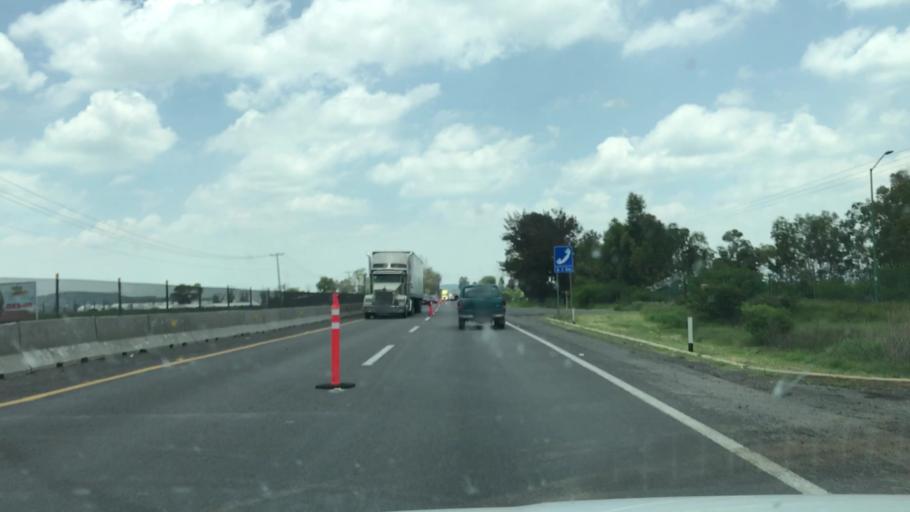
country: MX
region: Guanajuato
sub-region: Abasolo
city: San Bernardo Pena Blanca
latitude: 20.5006
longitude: -101.4792
